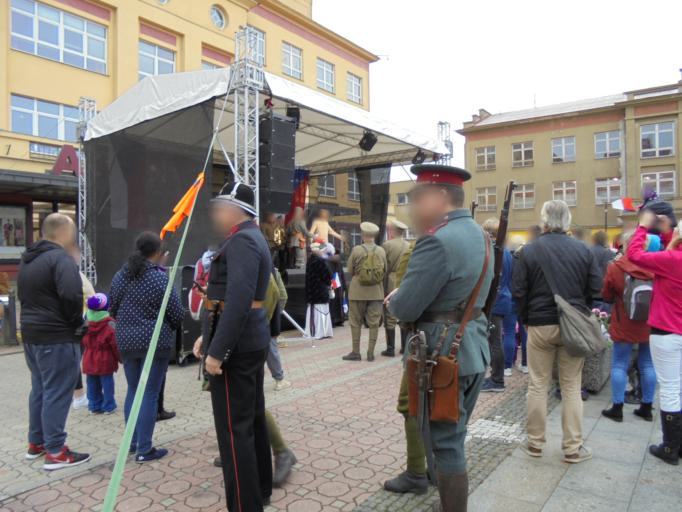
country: CZ
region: Moravskoslezsky
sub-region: Okres Ostrava-Mesto
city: Ostrava
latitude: 49.7915
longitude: 18.2399
